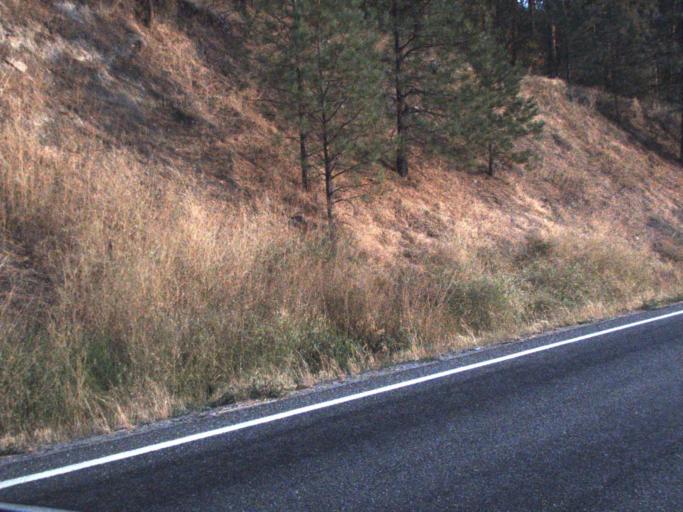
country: US
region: Washington
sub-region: Stevens County
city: Kettle Falls
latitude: 48.6990
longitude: -118.0141
